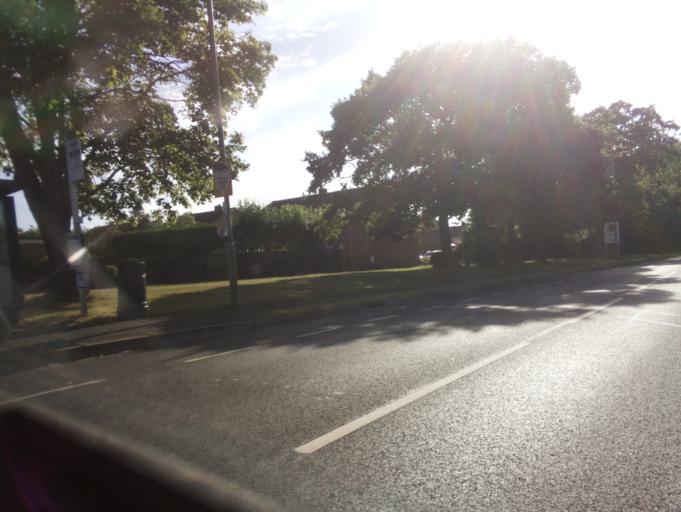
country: GB
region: England
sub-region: Hampshire
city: Romsey
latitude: 50.9861
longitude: -1.4661
